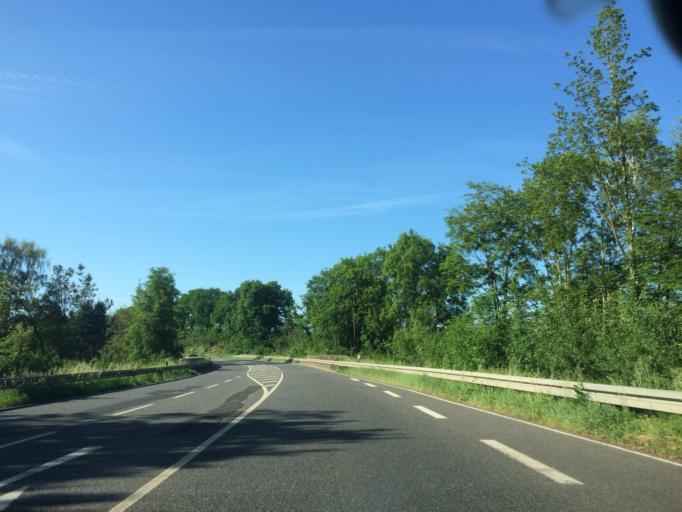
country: DE
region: Hesse
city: Grebenstein
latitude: 51.4422
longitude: 9.4095
